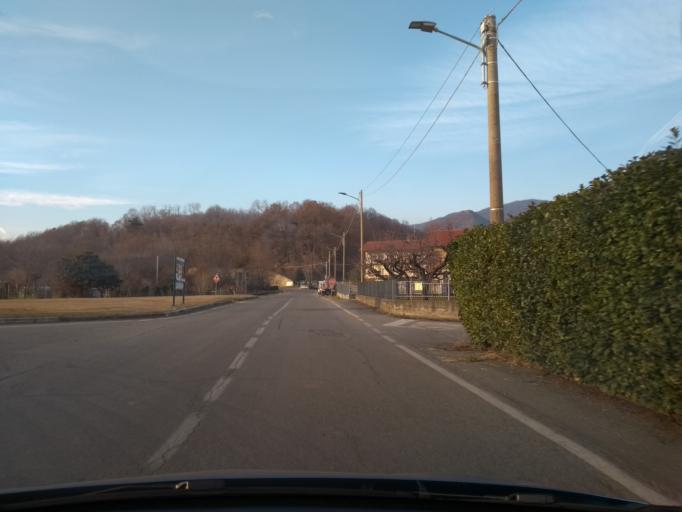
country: IT
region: Piedmont
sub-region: Provincia di Torino
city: Balangero
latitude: 45.2763
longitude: 7.5131
